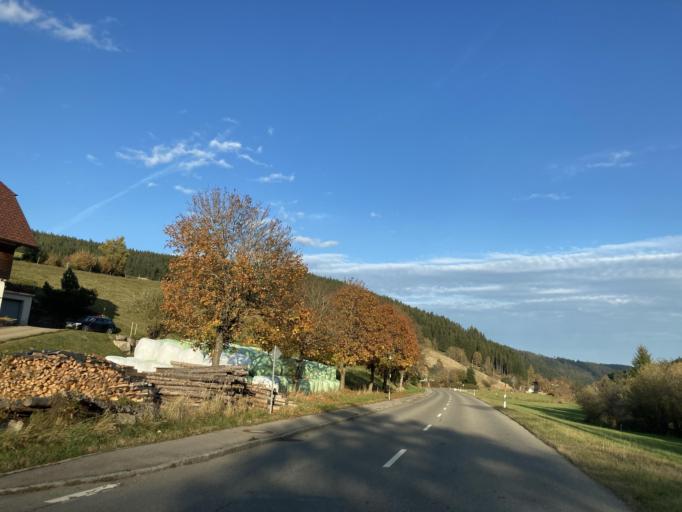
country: DE
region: Baden-Wuerttemberg
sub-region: Freiburg Region
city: Eisenbach
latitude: 48.0049
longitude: 8.2546
